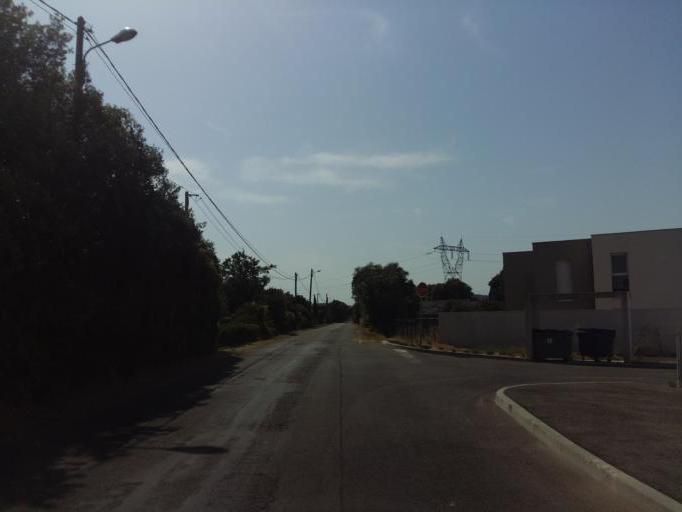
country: FR
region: Provence-Alpes-Cote d'Azur
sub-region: Departement du Vaucluse
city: Bollene
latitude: 44.2939
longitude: 4.7553
